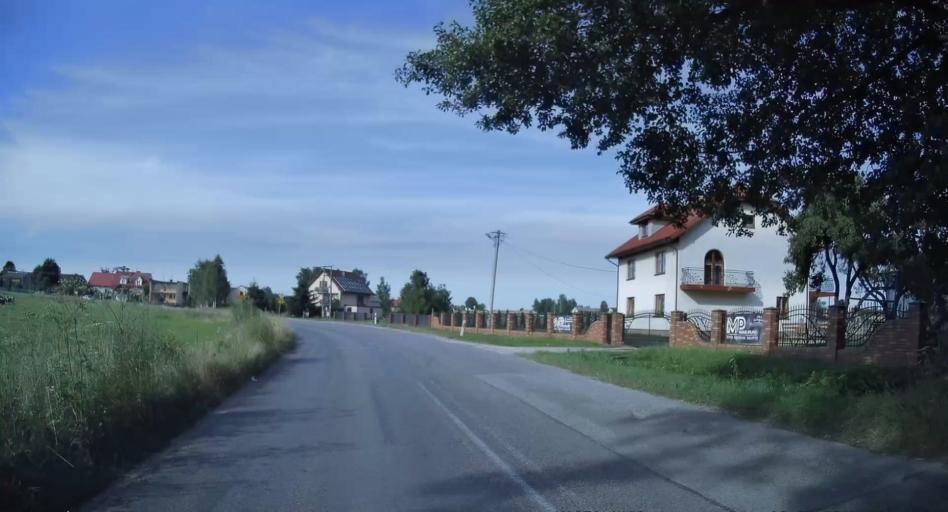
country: PL
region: Swietokrzyskie
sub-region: Powiat kielecki
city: Lopuszno
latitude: 50.9692
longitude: 20.2461
